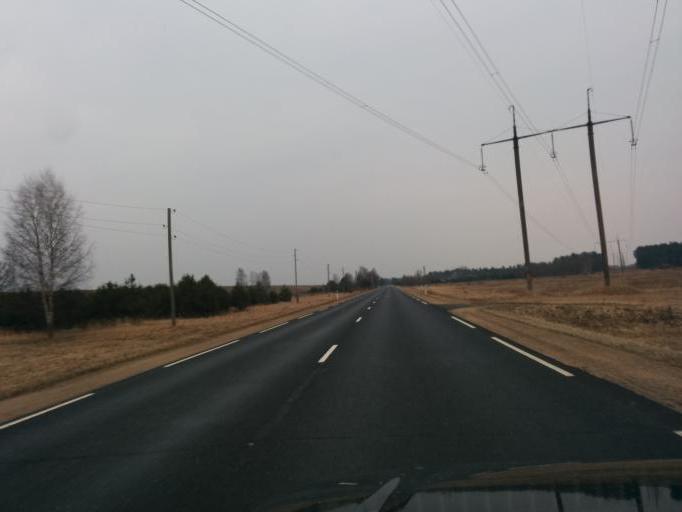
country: LV
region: Kekava
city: Kekava
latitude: 56.8200
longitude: 24.2980
